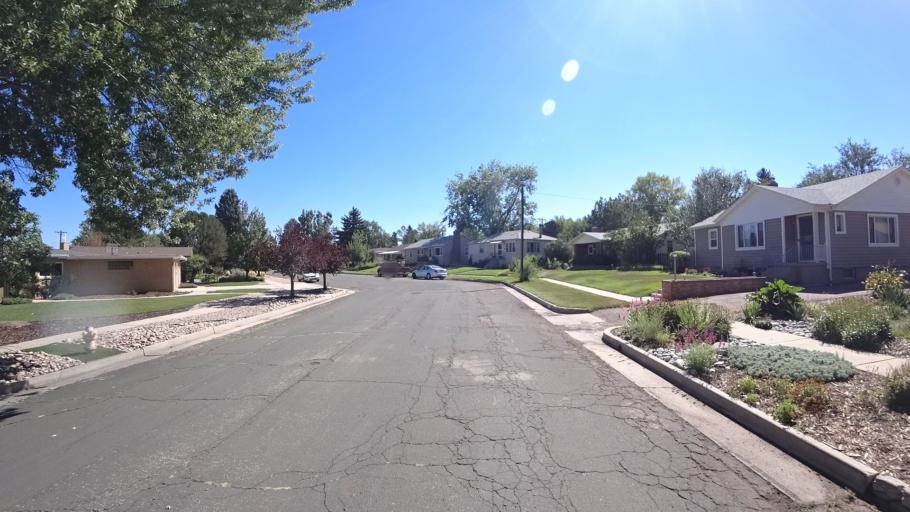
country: US
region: Colorado
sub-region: El Paso County
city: Colorado Springs
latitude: 38.8533
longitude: -104.7978
